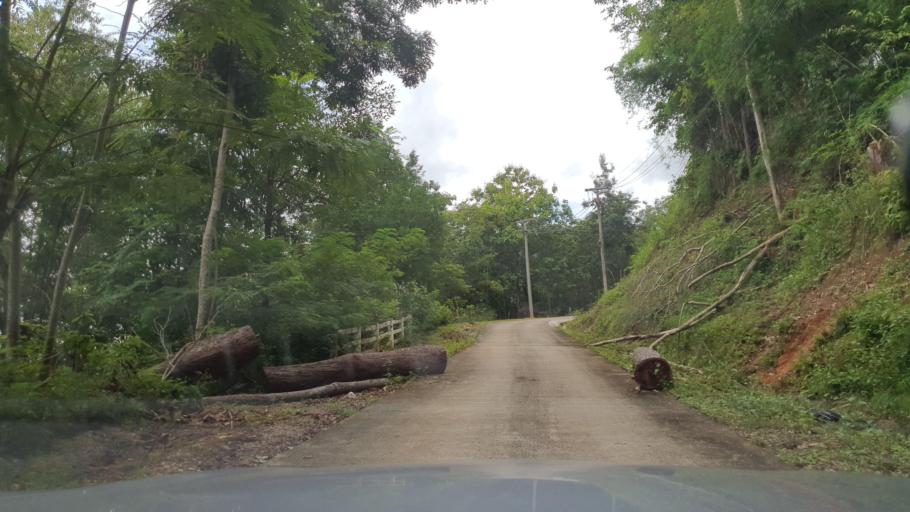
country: TH
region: Chiang Mai
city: Mae Wang
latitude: 18.6824
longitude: 98.6308
